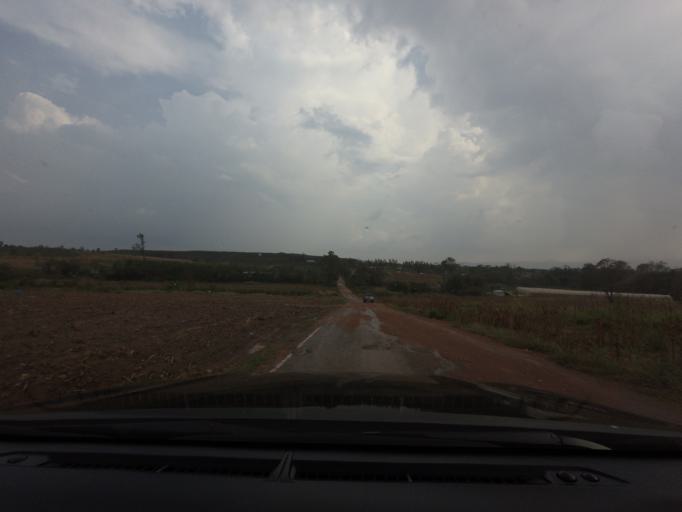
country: TH
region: Nakhon Ratchasima
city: Wang Nam Khiao
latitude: 14.4183
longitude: 101.7362
